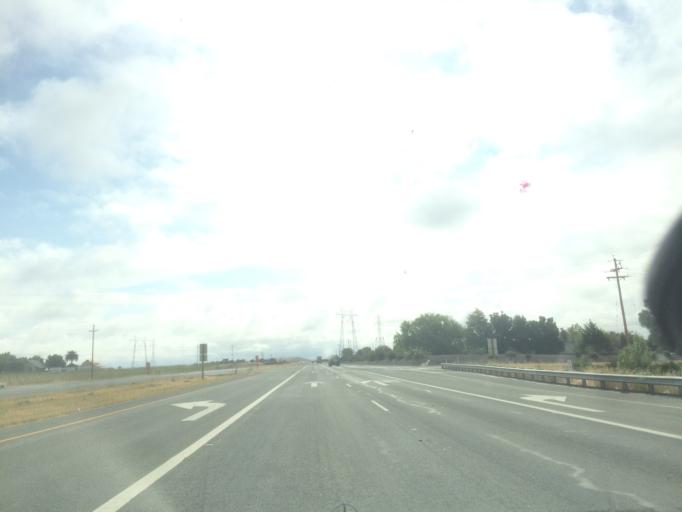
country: US
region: California
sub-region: San Luis Obispo County
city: Paso Robles
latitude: 35.6593
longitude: -120.5801
